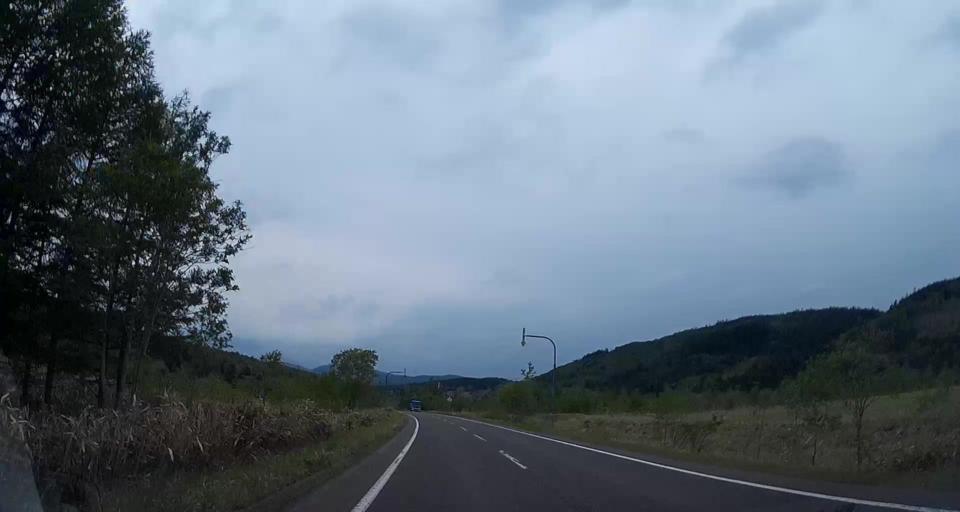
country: JP
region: Hokkaido
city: Shiraoi
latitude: 42.6760
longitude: 141.1497
